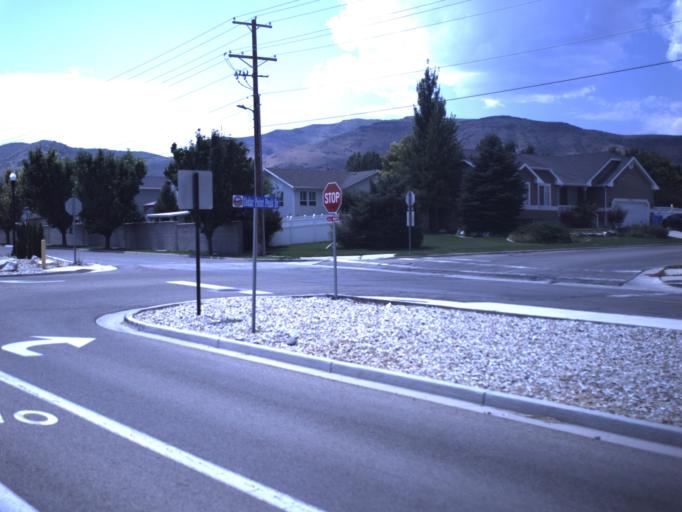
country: US
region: Utah
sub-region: Salt Lake County
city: Herriman
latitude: 40.5002
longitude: -112.0051
